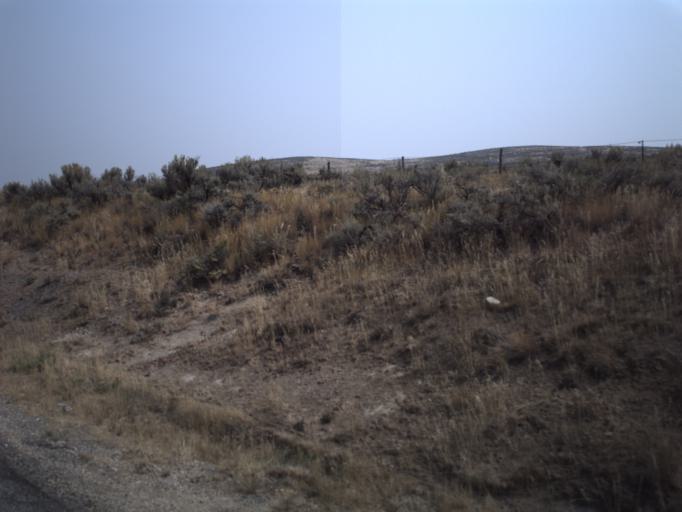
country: US
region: Utah
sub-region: Morgan County
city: Morgan
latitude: 40.9545
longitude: -111.5496
